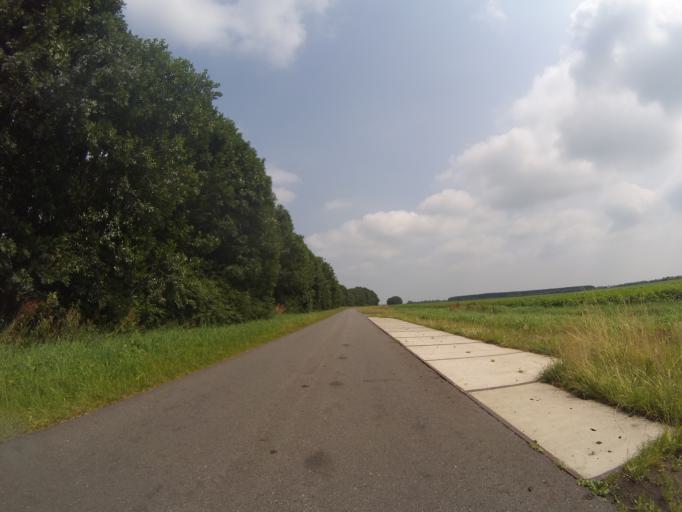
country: NL
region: Drenthe
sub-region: Gemeente Emmen
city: Emmen
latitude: 52.8595
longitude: 6.9494
